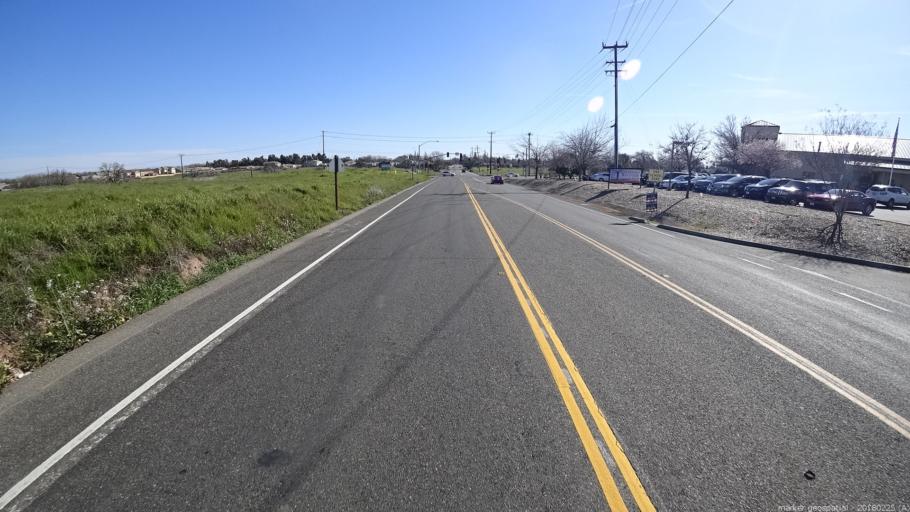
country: US
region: California
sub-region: Sacramento County
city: Antelope
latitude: 38.7288
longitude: -121.3660
